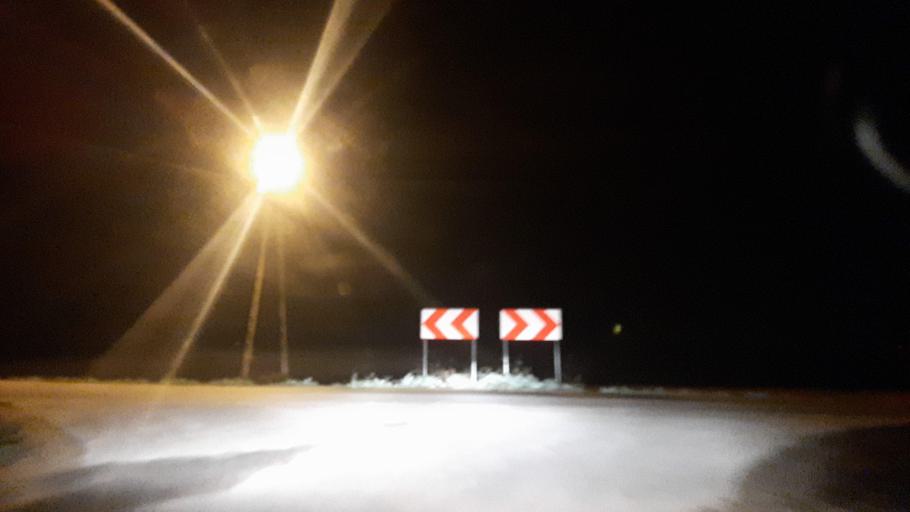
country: PL
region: Lublin Voivodeship
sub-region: Powiat lubelski
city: Garbow
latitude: 51.3877
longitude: 22.3425
